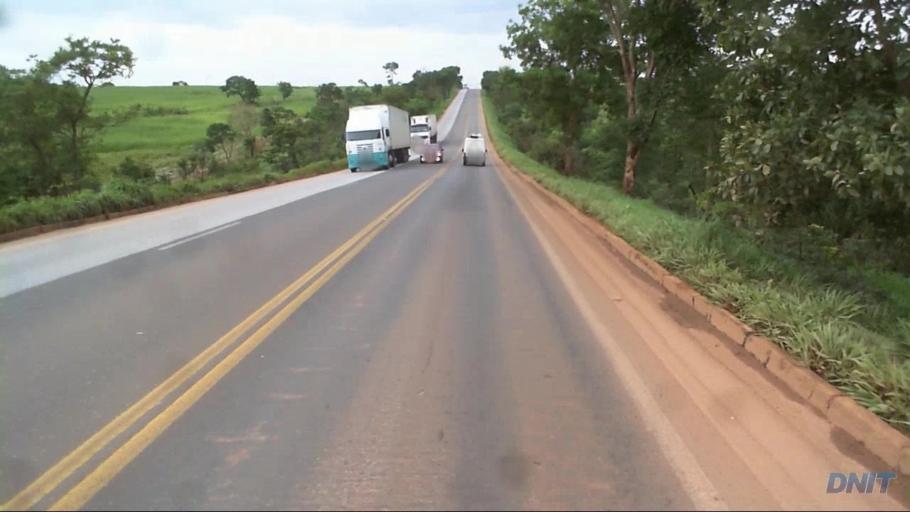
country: BR
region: Goias
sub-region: Uruacu
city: Uruacu
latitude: -14.5795
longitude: -49.1593
